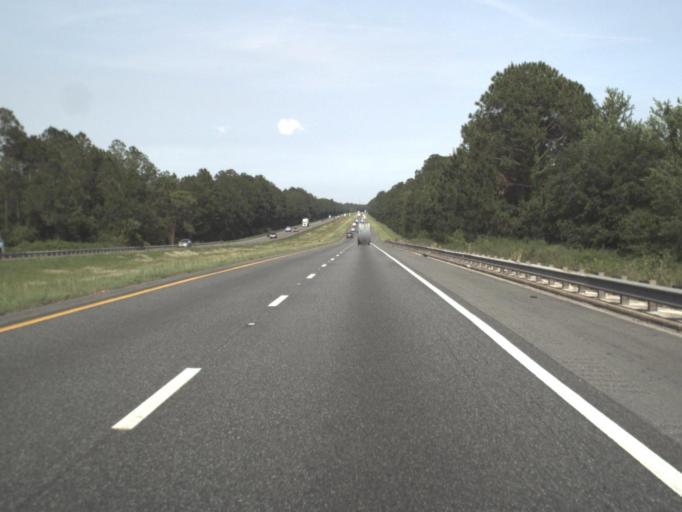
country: US
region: Florida
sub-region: Baker County
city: Macclenny
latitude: 30.2817
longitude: -82.0476
